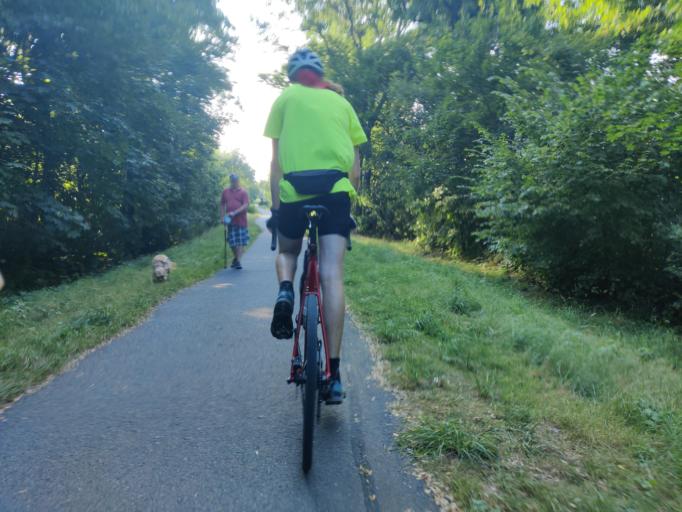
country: DE
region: Saxony
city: Bohlen
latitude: 51.2109
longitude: 12.3889
